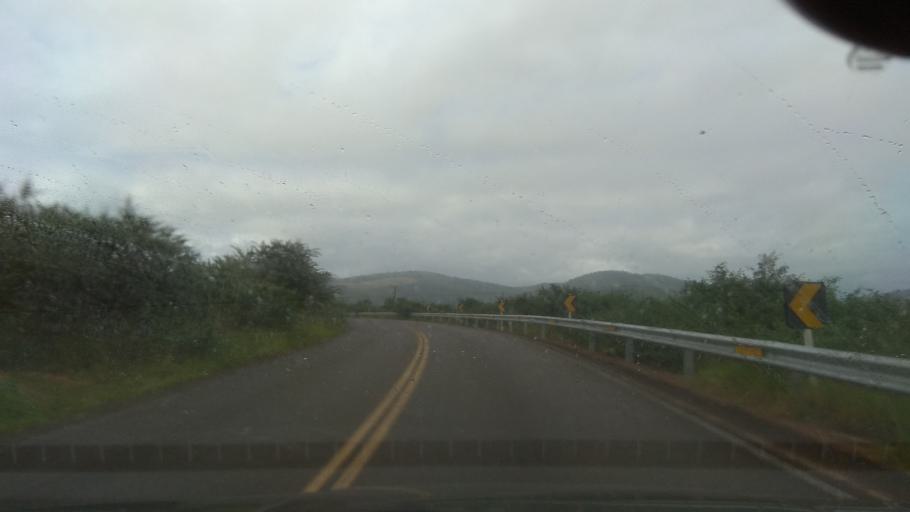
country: BR
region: Bahia
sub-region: Ubaira
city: Ubaira
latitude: -13.2478
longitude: -39.7390
